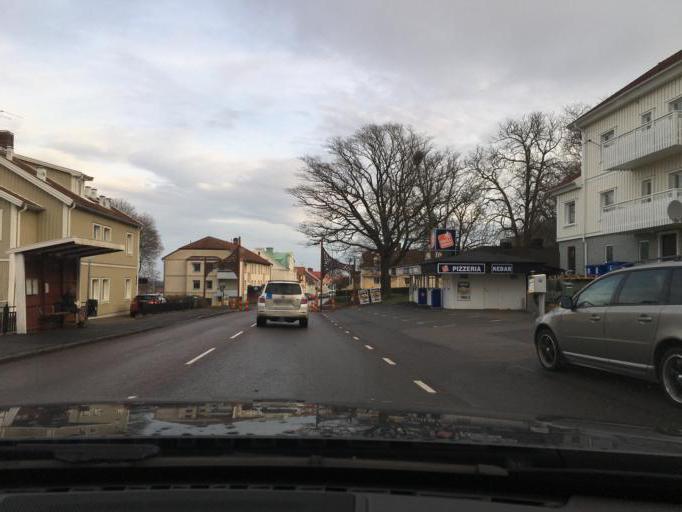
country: SE
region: Joenkoeping
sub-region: Jonkopings Kommun
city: Graenna
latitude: 58.0178
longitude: 14.4620
